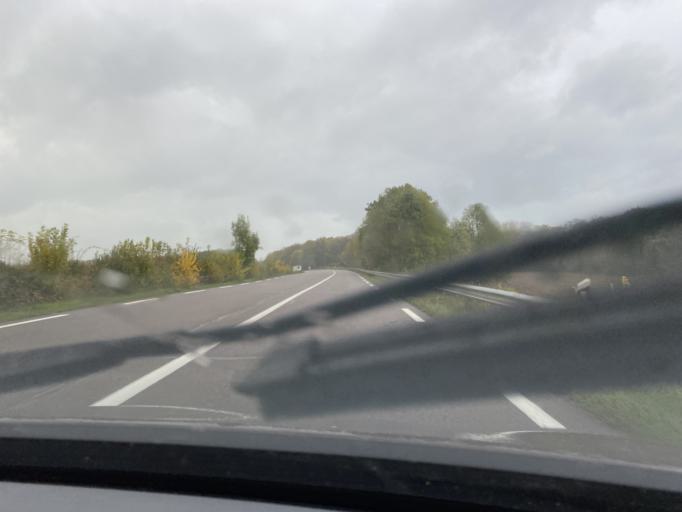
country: FR
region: Bourgogne
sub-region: Departement de la Cote-d'Or
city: Saulieu
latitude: 47.2962
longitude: 4.2163
